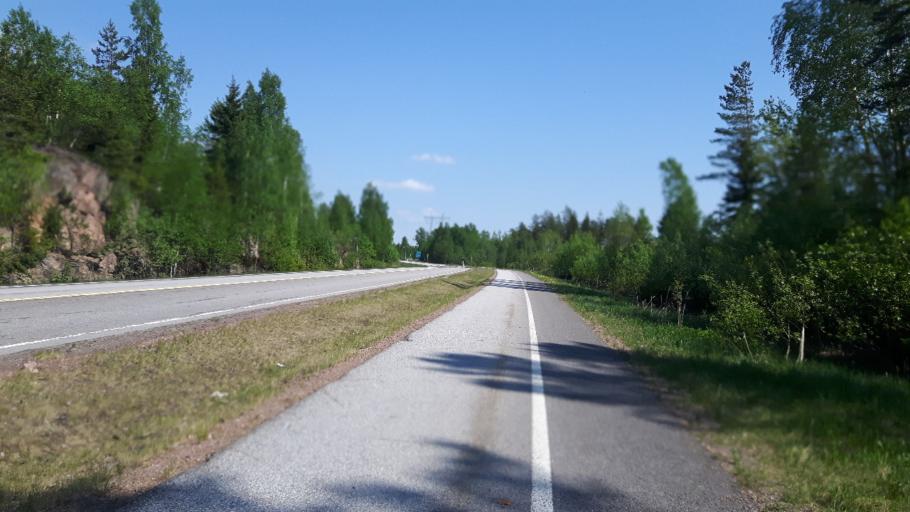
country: FI
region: Uusimaa
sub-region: Loviisa
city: Ruotsinpyhtaeae
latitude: 60.4874
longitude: 26.4112
